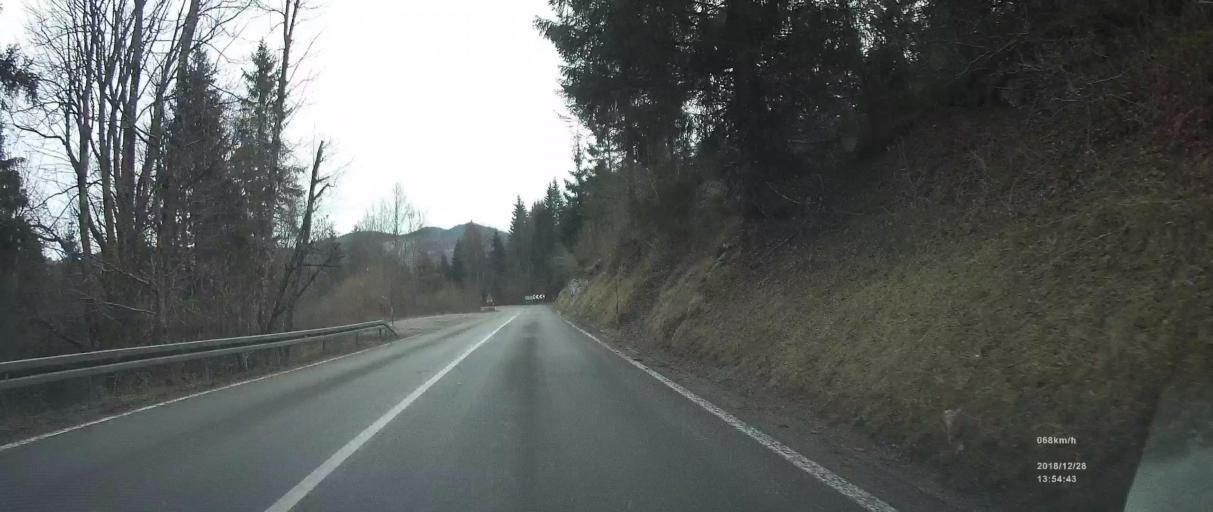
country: HR
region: Primorsko-Goranska
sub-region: Grad Delnice
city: Delnice
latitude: 45.3844
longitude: 14.8669
